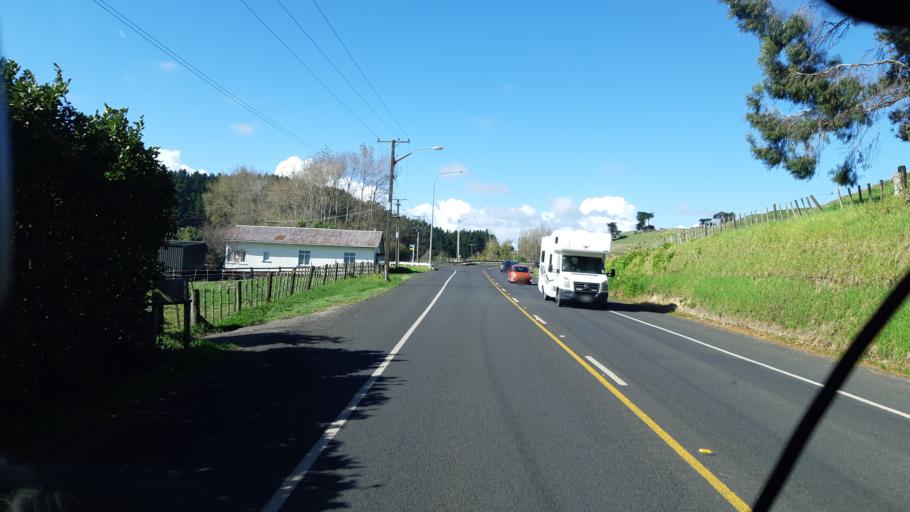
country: NZ
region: Manawatu-Wanganui
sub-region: Wanganui District
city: Wanganui
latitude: -39.9607
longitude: 175.0965
